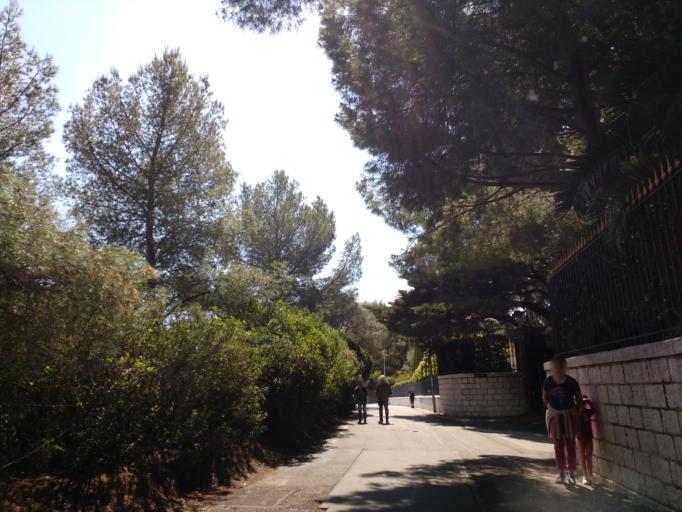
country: FR
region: Provence-Alpes-Cote d'Azur
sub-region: Departement des Alpes-Maritimes
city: Beaulieu-sur-Mer
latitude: 43.7027
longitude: 7.3220
